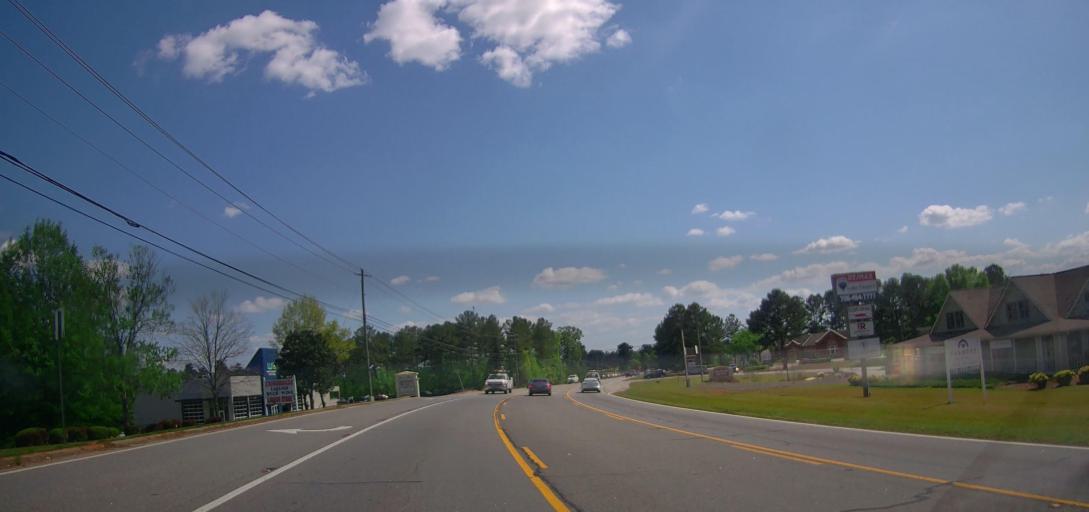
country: US
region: Georgia
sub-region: Putnam County
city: Jefferson
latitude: 33.4639
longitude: -83.2420
